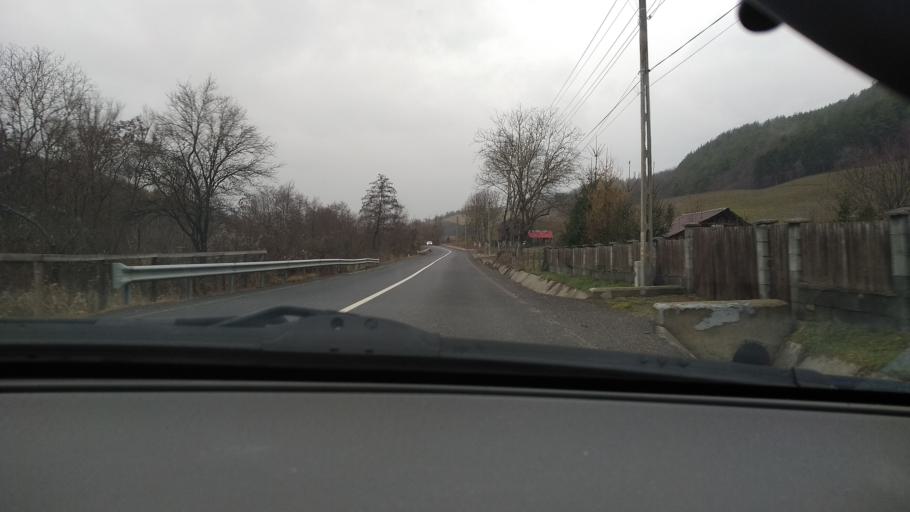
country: RO
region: Mures
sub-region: Comuna Magherani
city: Magherani
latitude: 46.5769
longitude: 24.9312
